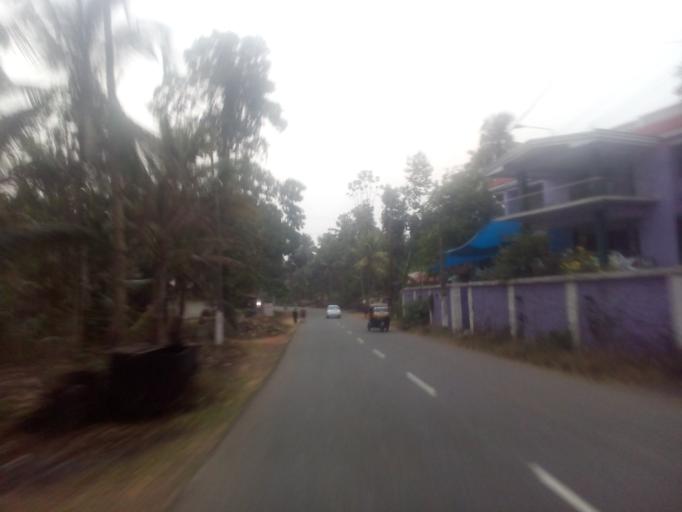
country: IN
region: Kerala
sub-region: Kottayam
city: Palackattumala
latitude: 9.8010
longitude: 76.6547
